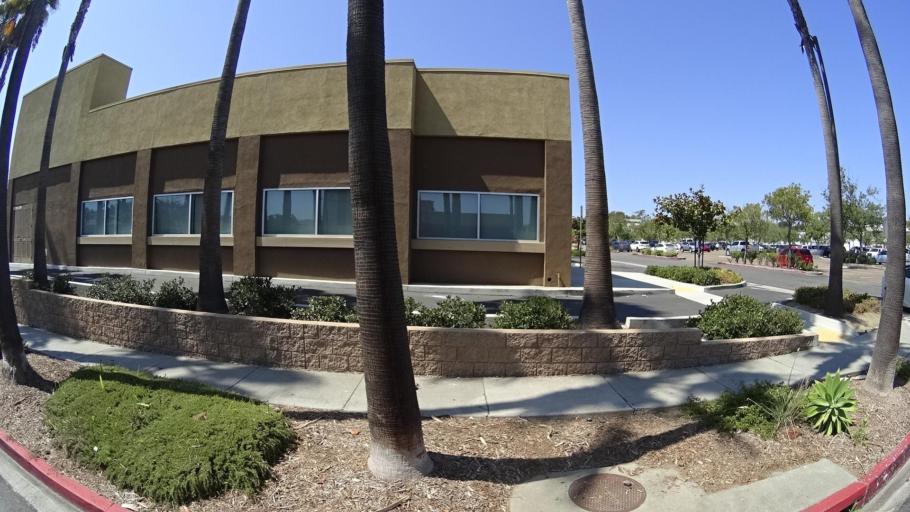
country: US
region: California
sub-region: San Diego County
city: Vista
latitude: 33.1710
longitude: -117.2156
